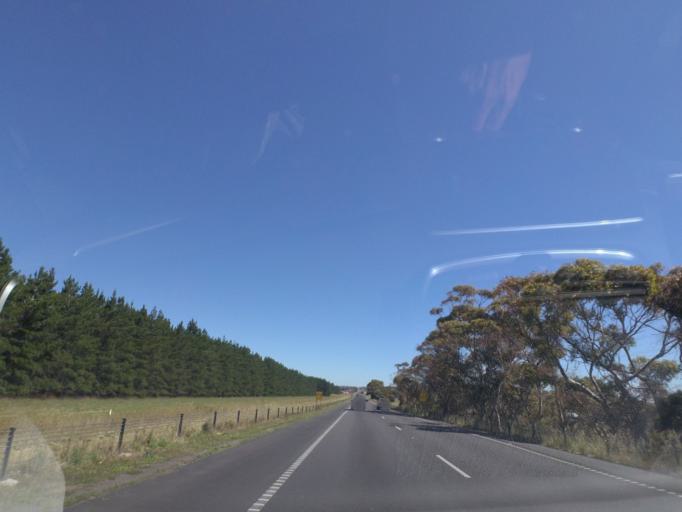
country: AU
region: Victoria
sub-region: Hume
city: Craigieburn
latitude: -37.5182
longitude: 144.9492
